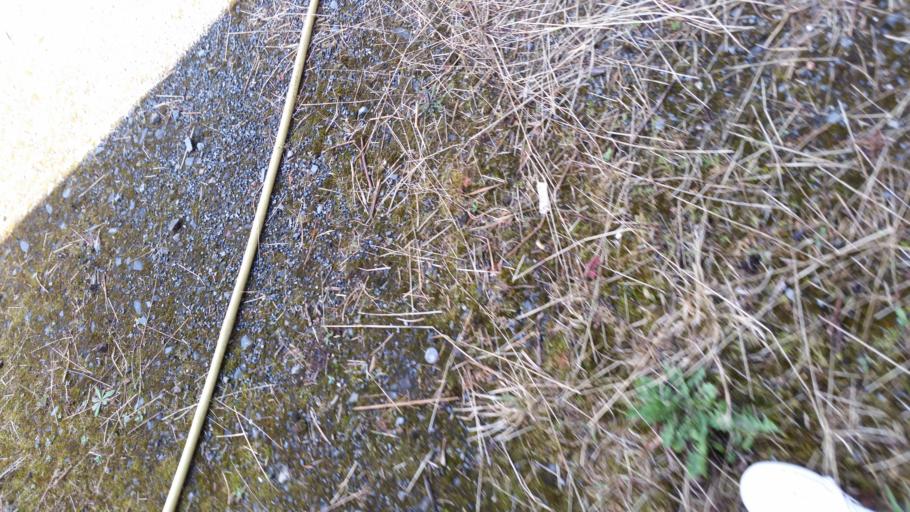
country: FR
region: Brittany
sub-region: Departement des Cotes-d'Armor
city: Pordic
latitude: 48.5797
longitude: -2.7985
